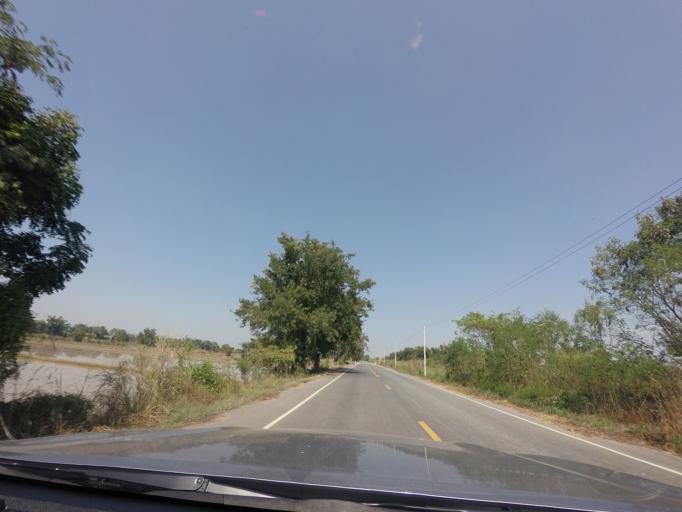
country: TH
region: Sukhothai
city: Sukhothai
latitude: 17.0813
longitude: 99.7907
